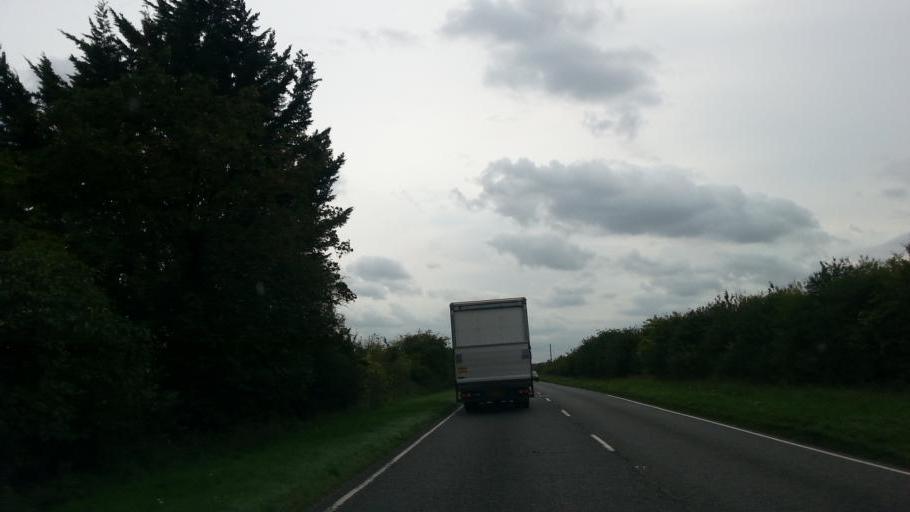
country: GB
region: England
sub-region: Cambridgeshire
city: Melbourn
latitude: 52.0541
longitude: 0.0218
